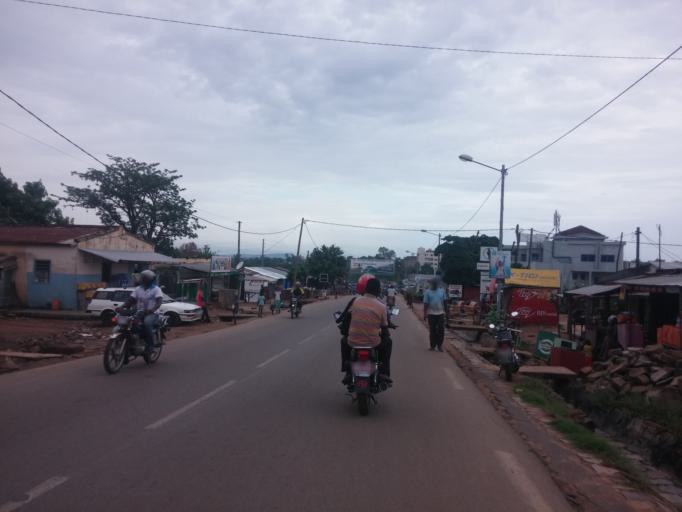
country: TG
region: Kara
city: Kara
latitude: 9.5498
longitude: 1.1997
